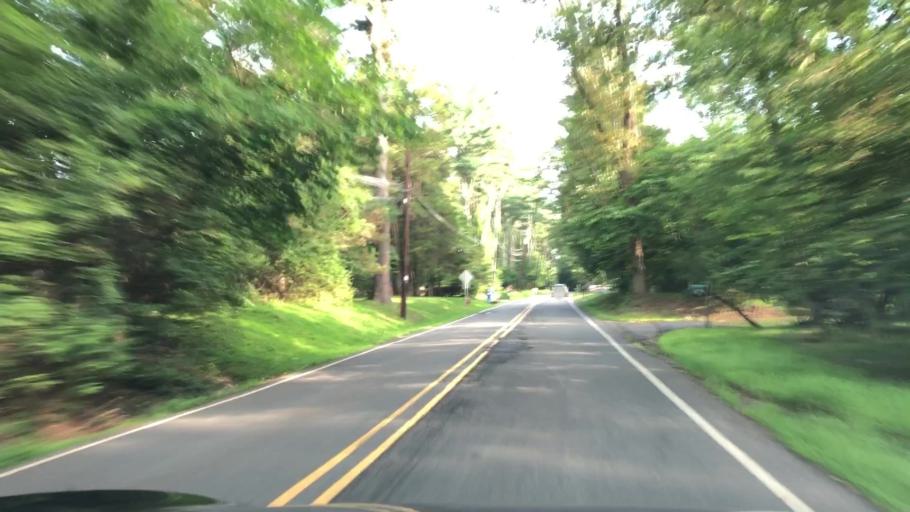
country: US
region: New Jersey
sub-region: Mercer County
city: Princeton
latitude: 40.3360
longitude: -74.7009
